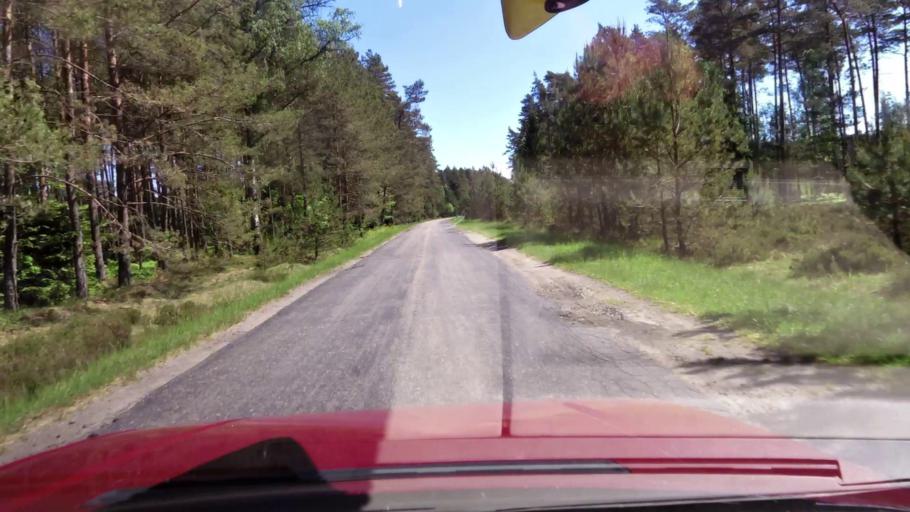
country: PL
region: West Pomeranian Voivodeship
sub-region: Powiat koszalinski
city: Bobolice
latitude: 54.0801
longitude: 16.4402
